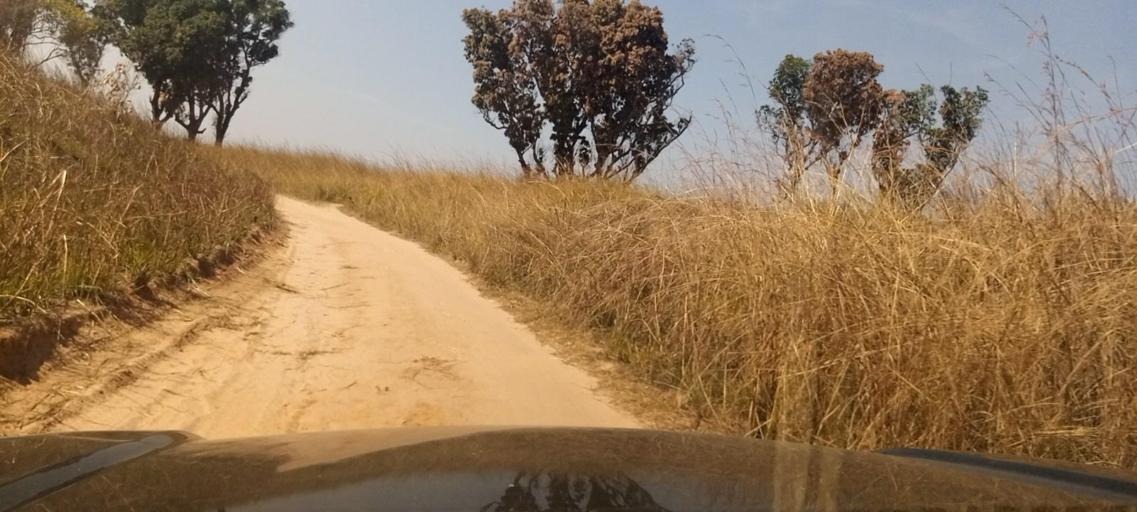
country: CD
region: Kasai-Oriental
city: Kabinda
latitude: -5.8031
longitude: 25.0284
